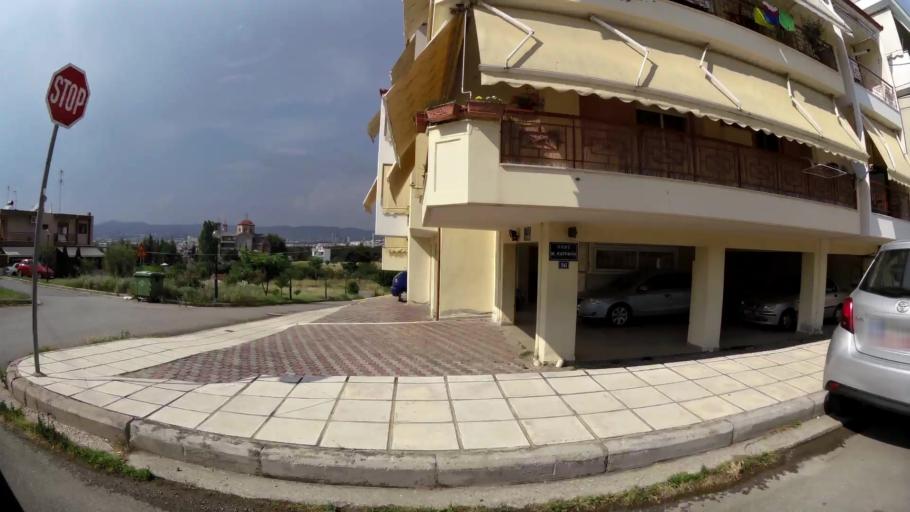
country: GR
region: Central Macedonia
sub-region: Nomos Thessalonikis
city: Polichni
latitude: 40.6694
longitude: 22.9478
